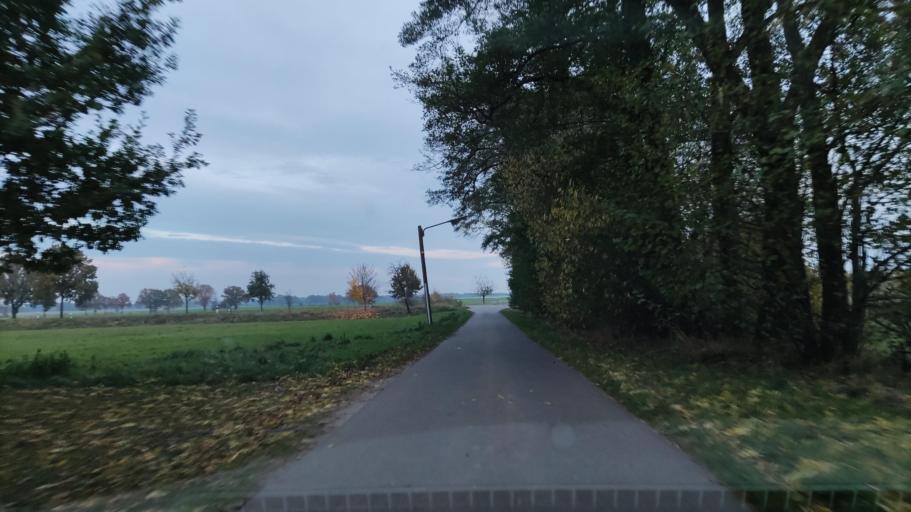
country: DE
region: Saxony-Anhalt
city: Jubar
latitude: 52.6465
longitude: 10.8726
